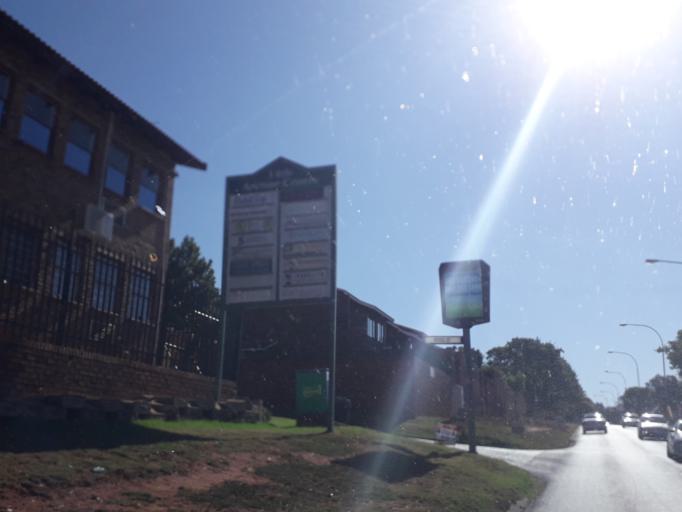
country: ZA
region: Gauteng
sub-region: City of Johannesburg Metropolitan Municipality
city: Roodepoort
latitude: -26.1514
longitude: 27.9417
